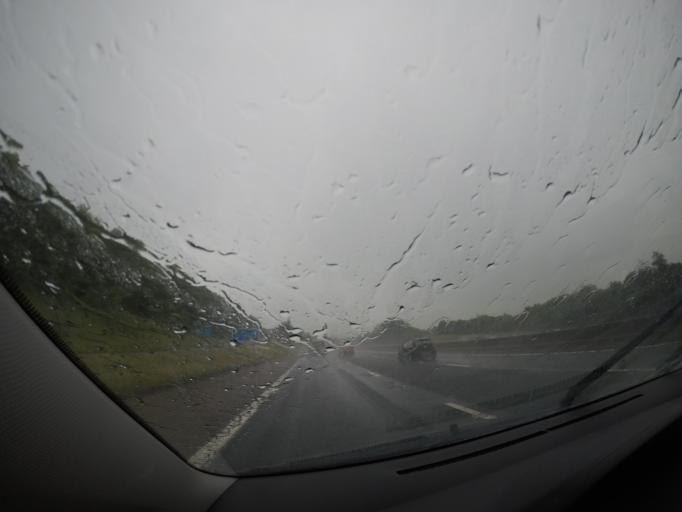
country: GB
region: England
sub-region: Cumbria
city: Penrith
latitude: 54.6909
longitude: -2.7917
